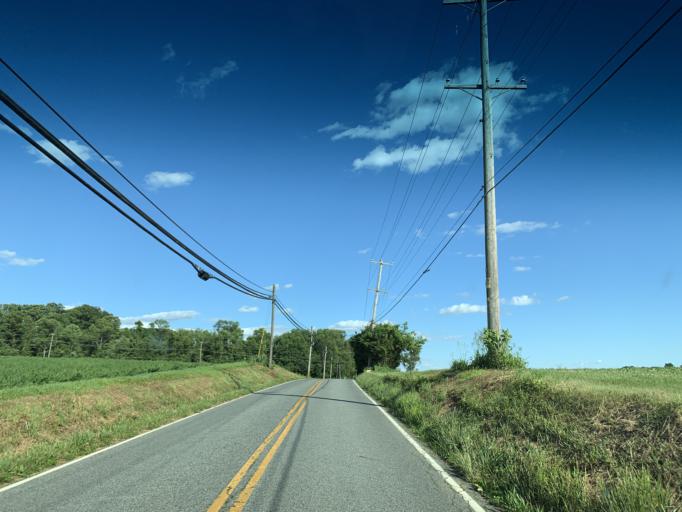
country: US
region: Maryland
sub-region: Cecil County
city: Perryville
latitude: 39.5967
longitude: -76.0904
